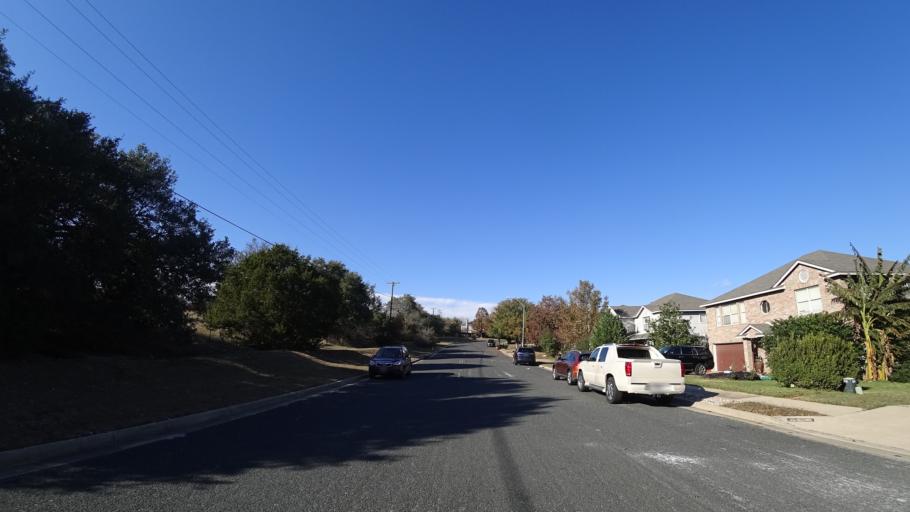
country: US
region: Texas
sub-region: Williamson County
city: Brushy Creek
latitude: 30.4855
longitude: -97.7432
